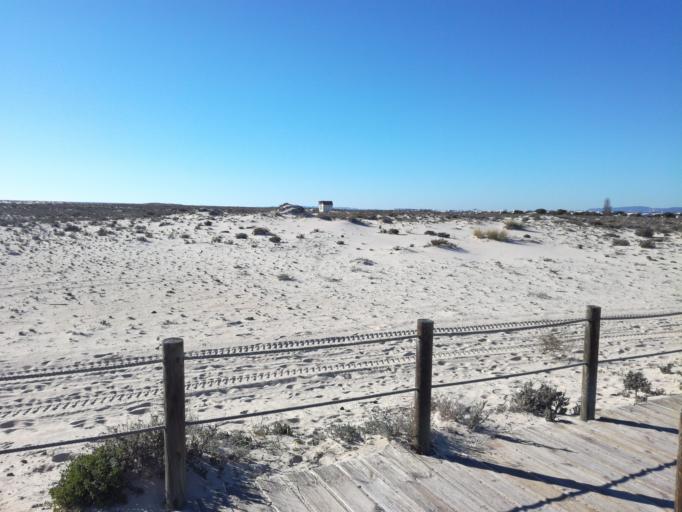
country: PT
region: Faro
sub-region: Olhao
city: Olhao
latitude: 37.0143
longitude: -7.7967
